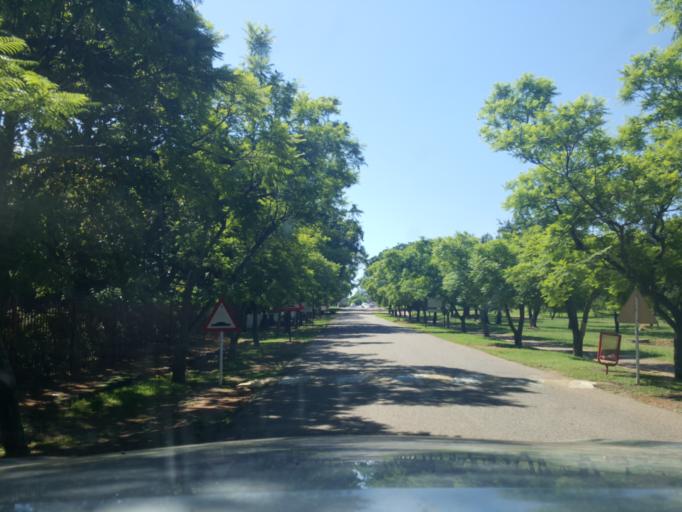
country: ZA
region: Gauteng
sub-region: City of Tshwane Metropolitan Municipality
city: Cullinan
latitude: -25.6708
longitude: 28.5171
